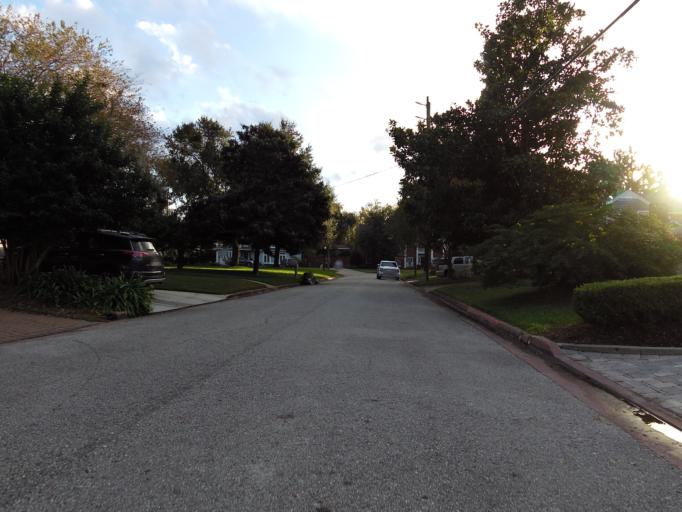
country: US
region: Florida
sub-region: Duval County
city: Jacksonville
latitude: 30.2826
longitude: -81.6610
